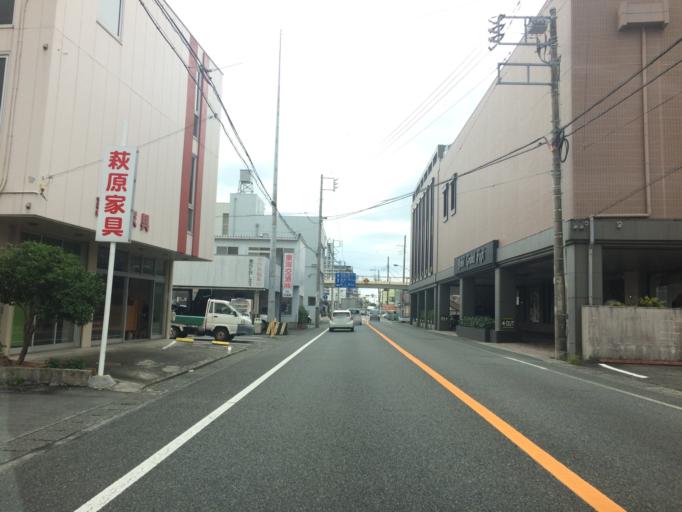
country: JP
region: Shizuoka
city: Fuji
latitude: 35.1556
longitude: 138.6487
